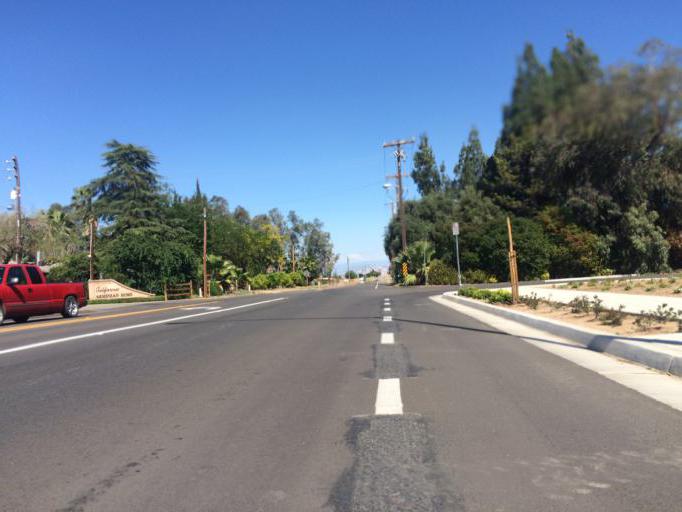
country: US
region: California
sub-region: Fresno County
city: Sunnyside
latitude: 36.7369
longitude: -119.6692
